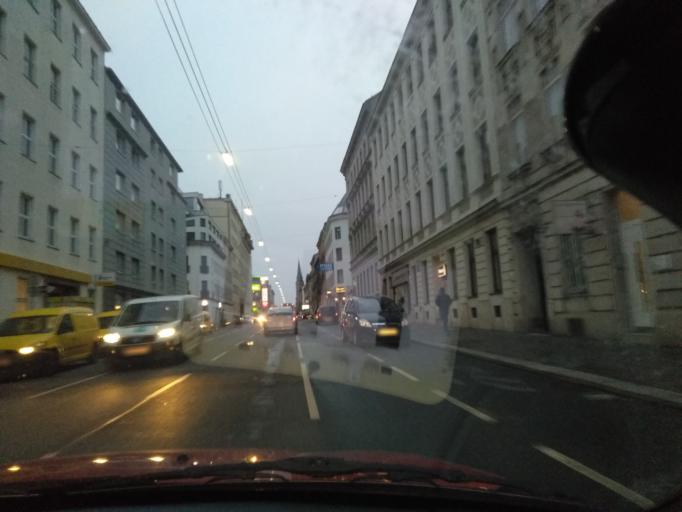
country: AT
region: Vienna
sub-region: Wien Stadt
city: Vienna
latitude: 48.2190
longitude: 16.3204
